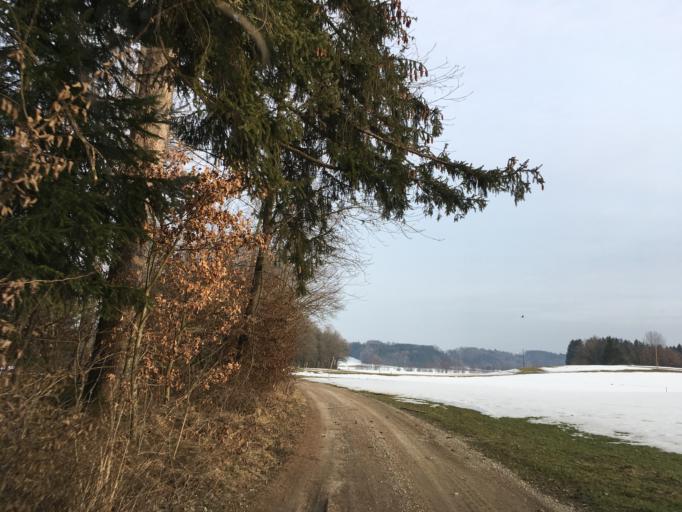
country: DE
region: Bavaria
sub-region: Upper Bavaria
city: Halfing
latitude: 47.9429
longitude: 12.2665
